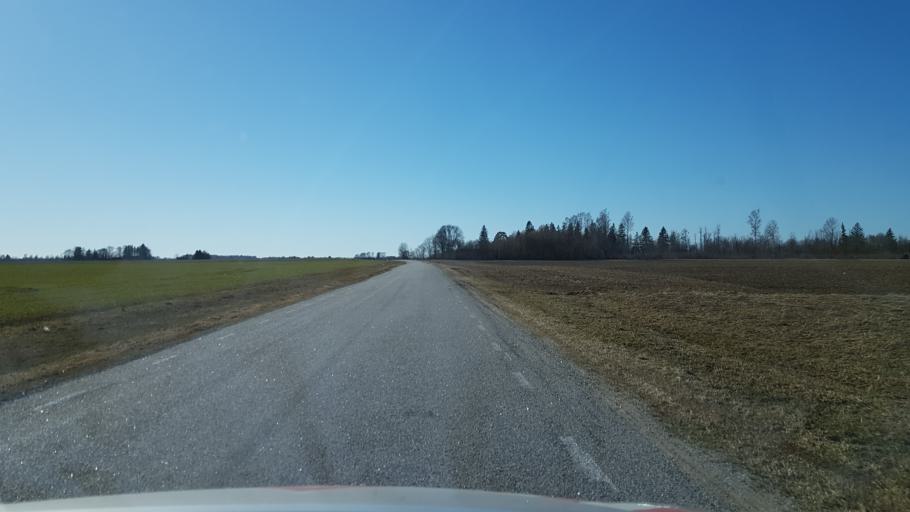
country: EE
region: Laeaene-Virumaa
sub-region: Haljala vald
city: Haljala
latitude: 59.4337
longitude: 26.2353
